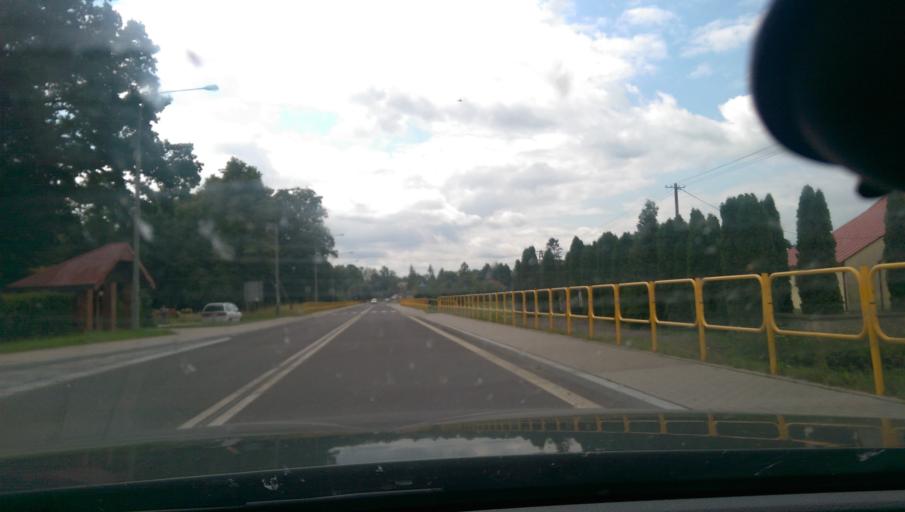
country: PL
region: Warmian-Masurian Voivodeship
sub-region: Powiat olecki
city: Kowale Oleckie
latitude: 54.2109
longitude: 22.4125
